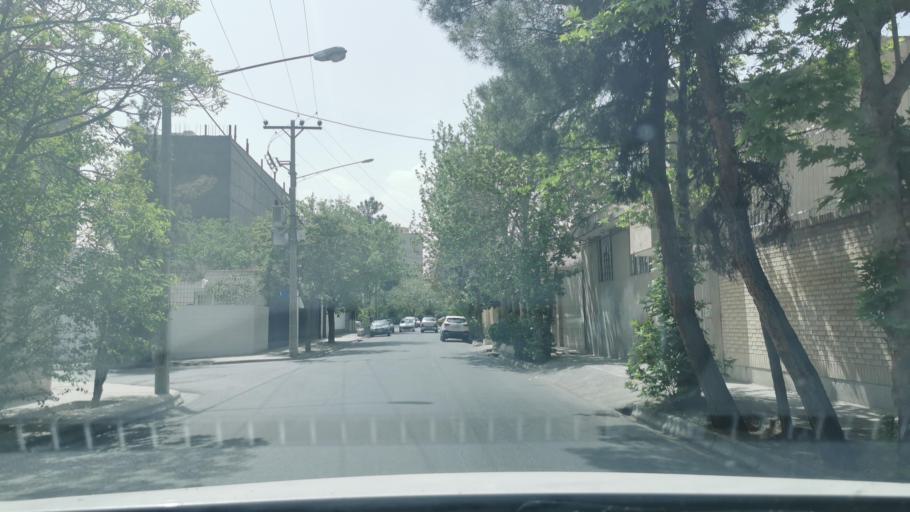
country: IR
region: Razavi Khorasan
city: Mashhad
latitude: 36.3351
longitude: 59.4810
